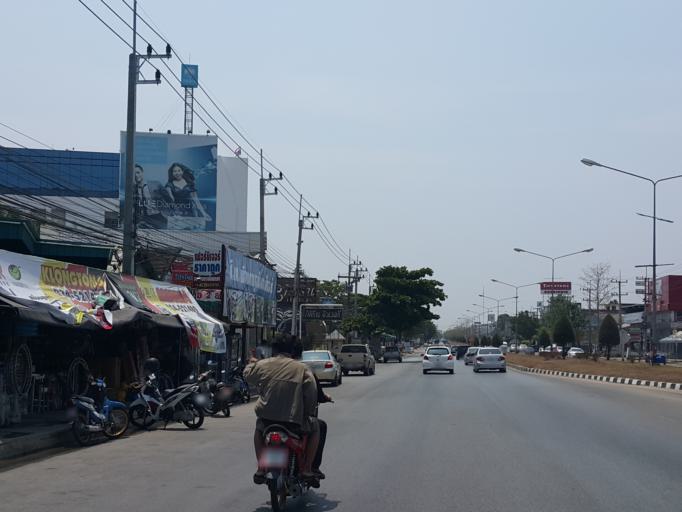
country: TH
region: Kanchanaburi
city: Kanchanaburi
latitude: 14.0457
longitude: 99.5103
